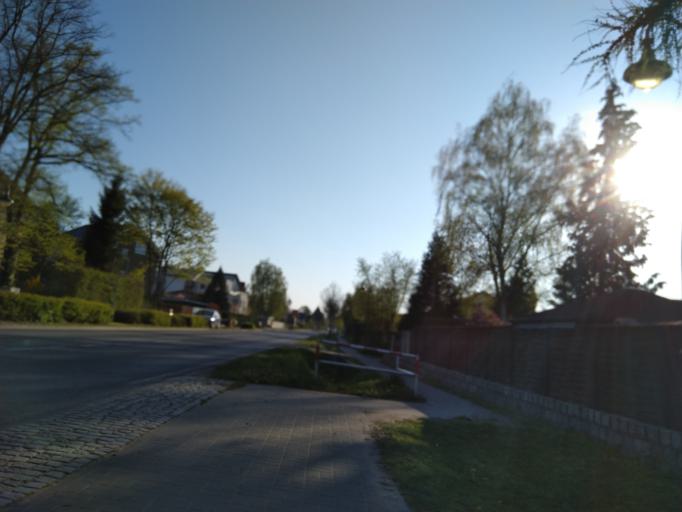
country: DE
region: Berlin
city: Buch
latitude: 52.6482
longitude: 13.5335
